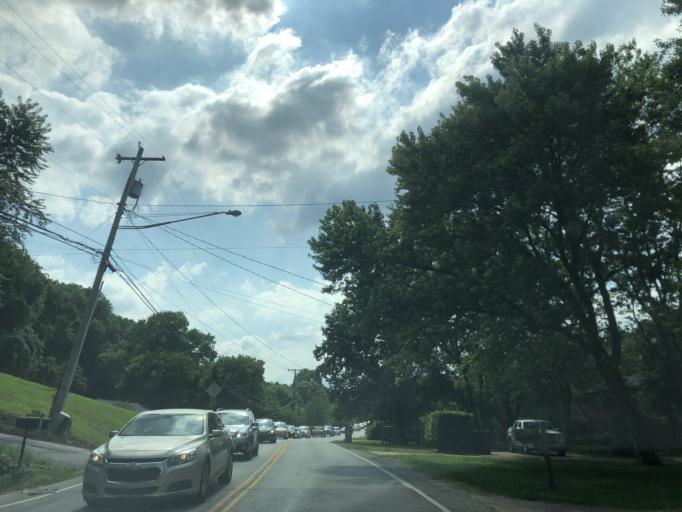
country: US
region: Tennessee
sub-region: Davidson County
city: Oak Hill
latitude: 36.0743
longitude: -86.7360
